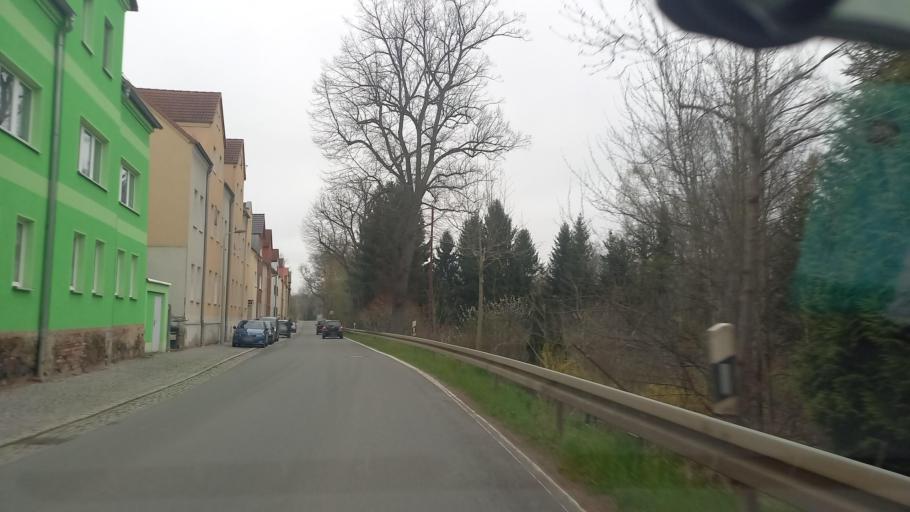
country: DE
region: Saxony
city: Wilkau-Hasslau
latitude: 50.7033
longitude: 12.5212
